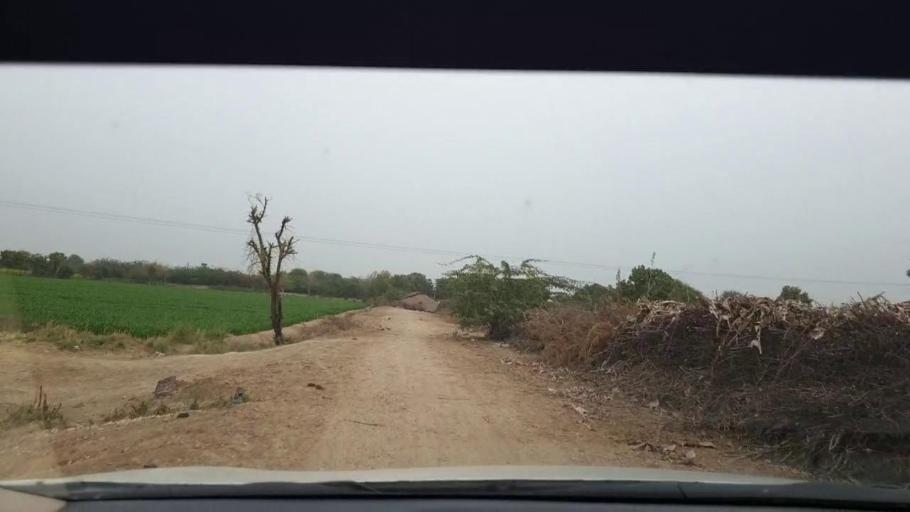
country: PK
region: Sindh
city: Berani
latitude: 25.8840
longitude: 68.8092
